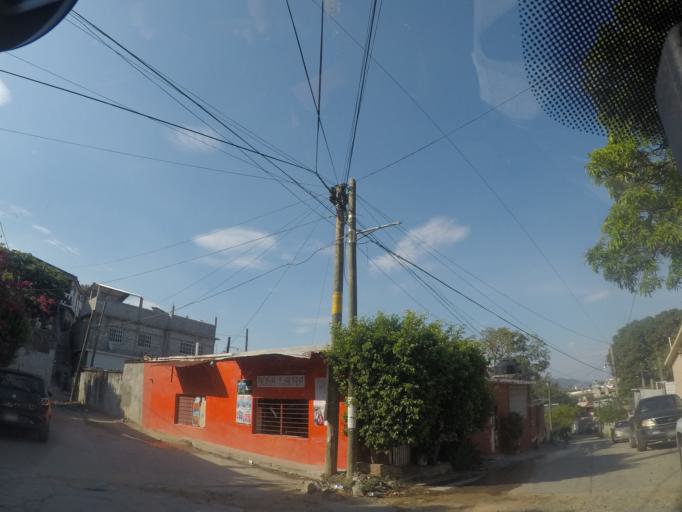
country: MX
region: Oaxaca
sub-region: Salina Cruz
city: Salina Cruz
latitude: 16.1972
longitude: -95.2038
